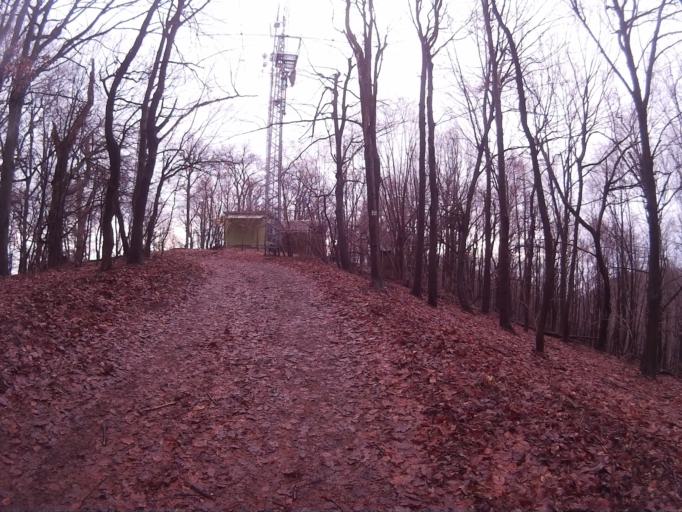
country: HU
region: Nograd
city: Somoskoujfalu
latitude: 48.1564
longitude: 19.7895
